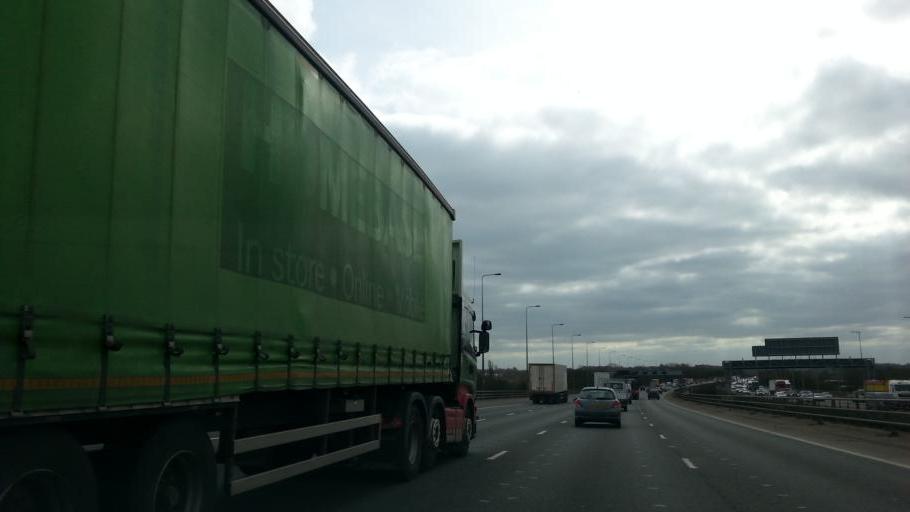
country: GB
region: England
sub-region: Warrington
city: Lymm
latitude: 53.3872
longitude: -2.5047
